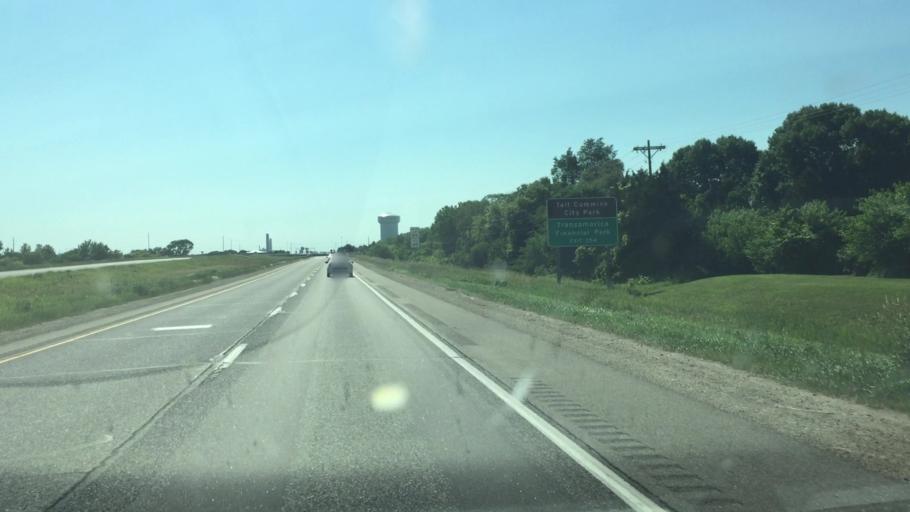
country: US
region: Iowa
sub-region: Linn County
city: Ely
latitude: 41.9267
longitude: -91.6286
